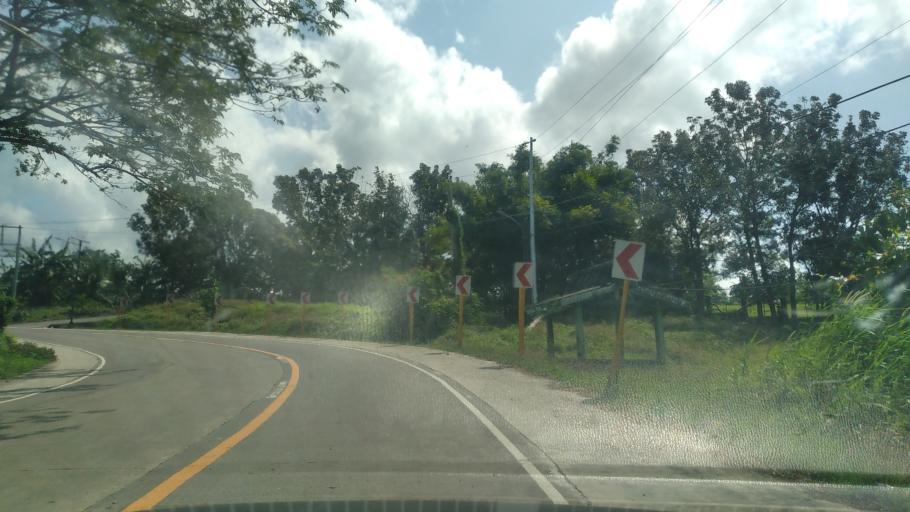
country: PH
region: Calabarzon
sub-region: Province of Quezon
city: Unisan
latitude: 13.8347
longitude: 121.9838
